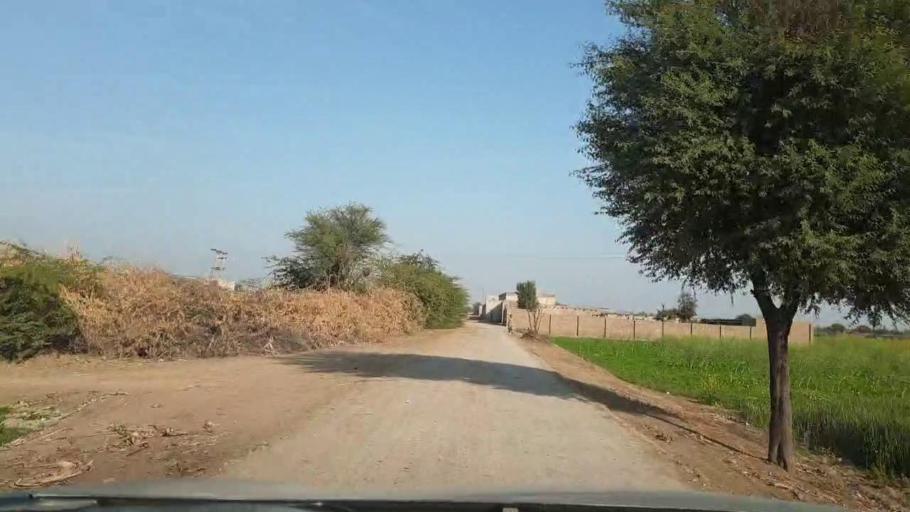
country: PK
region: Sindh
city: Berani
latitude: 25.7270
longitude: 68.7823
